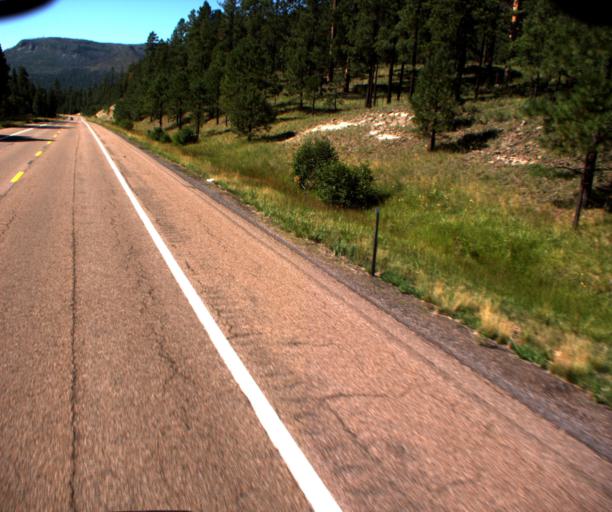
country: US
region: Arizona
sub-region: Apache County
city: Eagar
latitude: 33.8751
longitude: -109.1658
